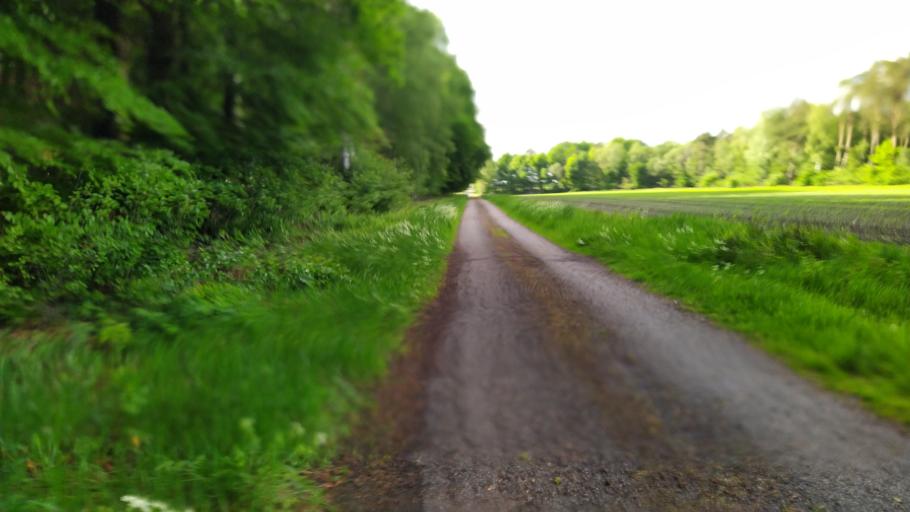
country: DE
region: Lower Saxony
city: Farven
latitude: 53.4436
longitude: 9.2844
